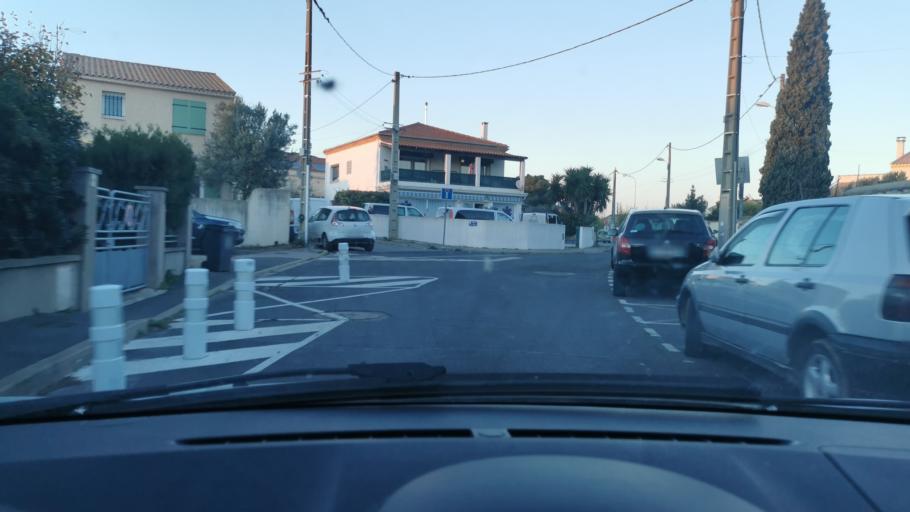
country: FR
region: Languedoc-Roussillon
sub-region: Departement de l'Herault
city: Frontignan
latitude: 43.4528
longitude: 3.7562
